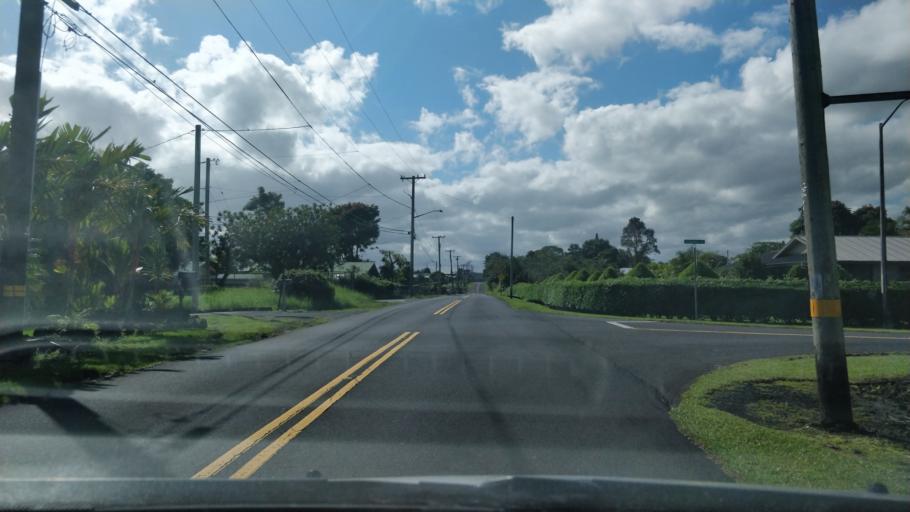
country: US
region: Hawaii
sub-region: Hawaii County
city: Hilo
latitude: 19.6781
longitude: -155.1062
